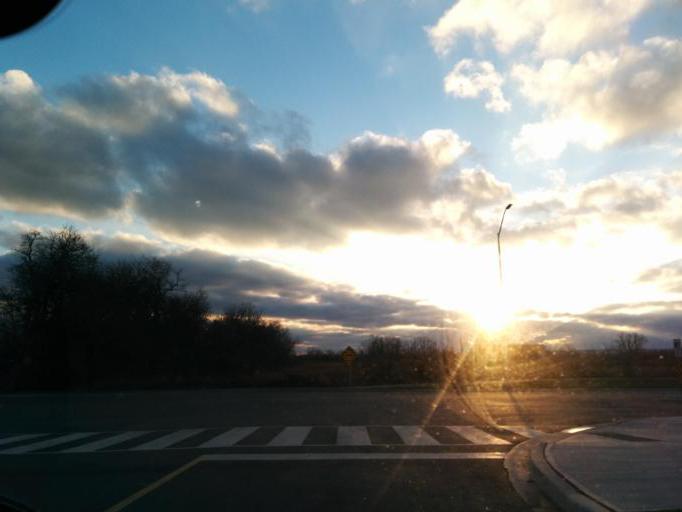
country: CA
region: Ontario
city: Oakville
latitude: 43.4483
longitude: -79.7650
